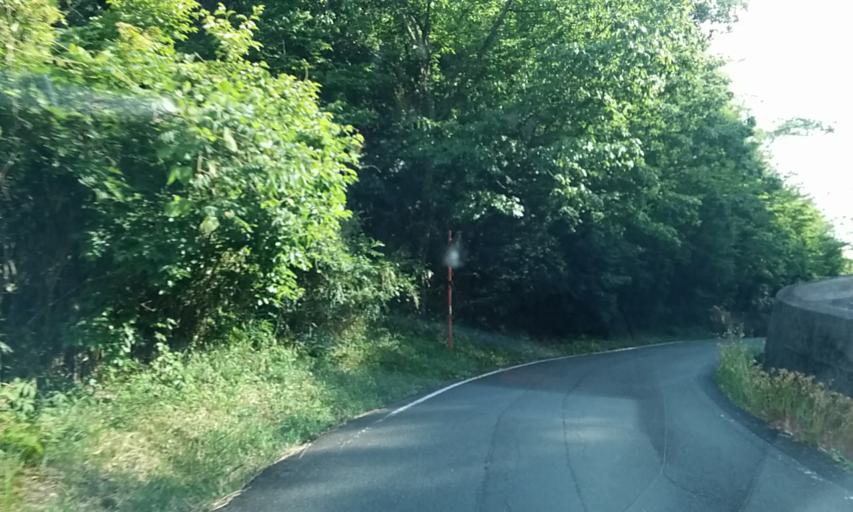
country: JP
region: Kyoto
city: Ayabe
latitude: 35.3355
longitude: 135.2985
